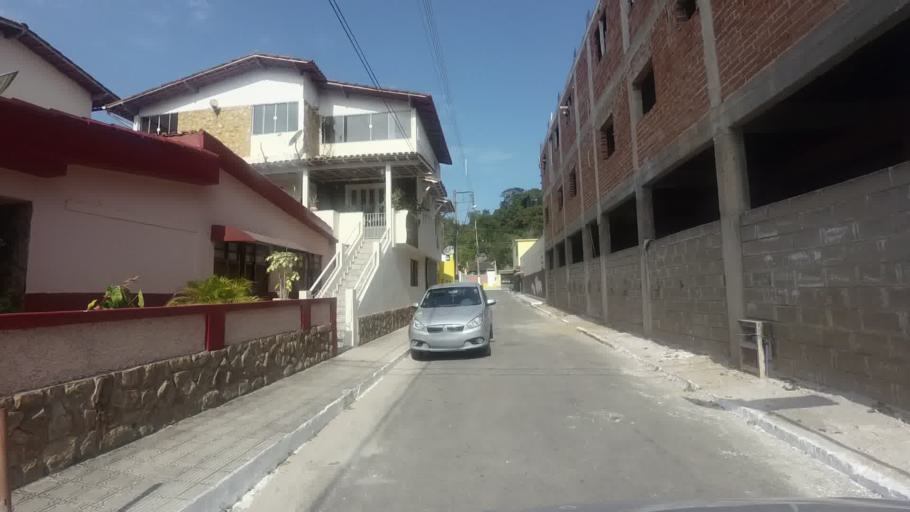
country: BR
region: Espirito Santo
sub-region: Itapemirim
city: Itapemirim
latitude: -21.0080
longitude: -40.8344
